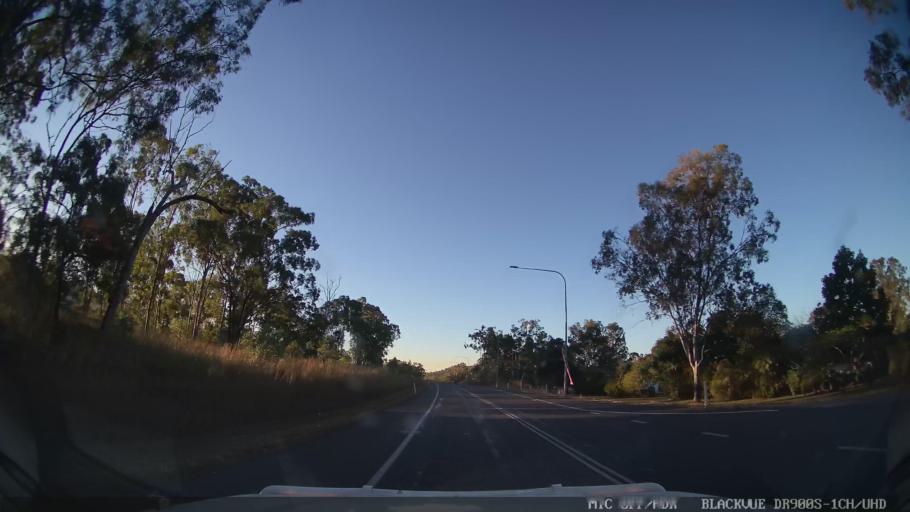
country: AU
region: Queensland
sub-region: Gladstone
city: Toolooa
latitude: -23.9557
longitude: 151.2202
